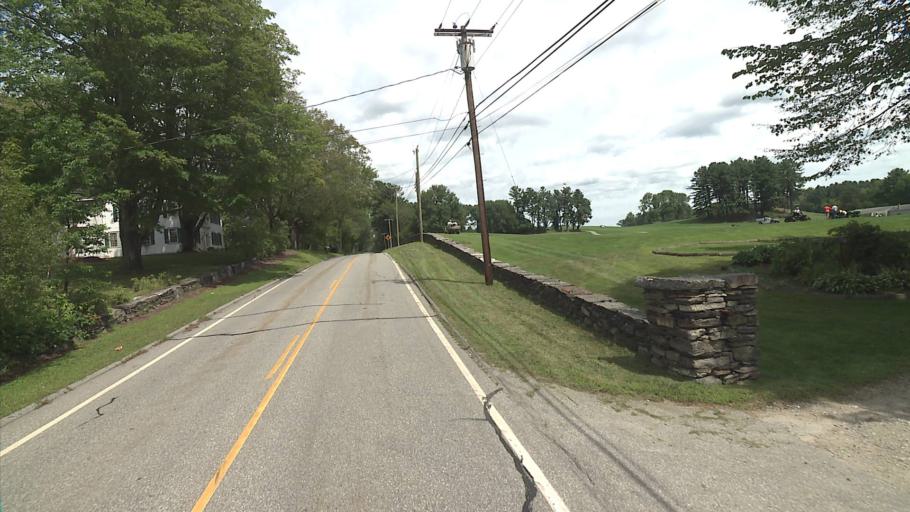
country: US
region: Connecticut
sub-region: Windham County
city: Thompson
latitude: 41.9377
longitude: -71.8662
